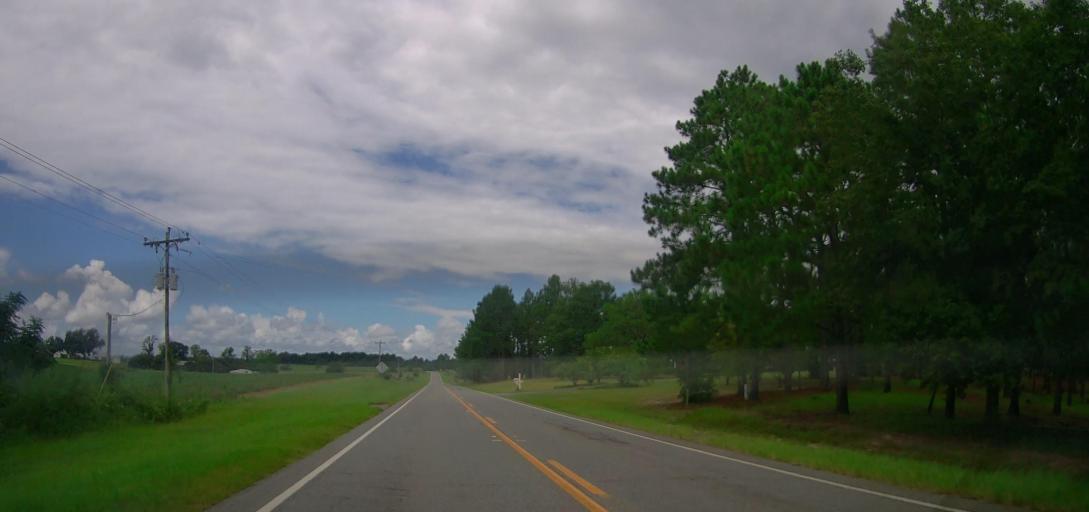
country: US
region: Georgia
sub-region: Wilcox County
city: Rochelle
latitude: 32.0256
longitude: -83.5658
